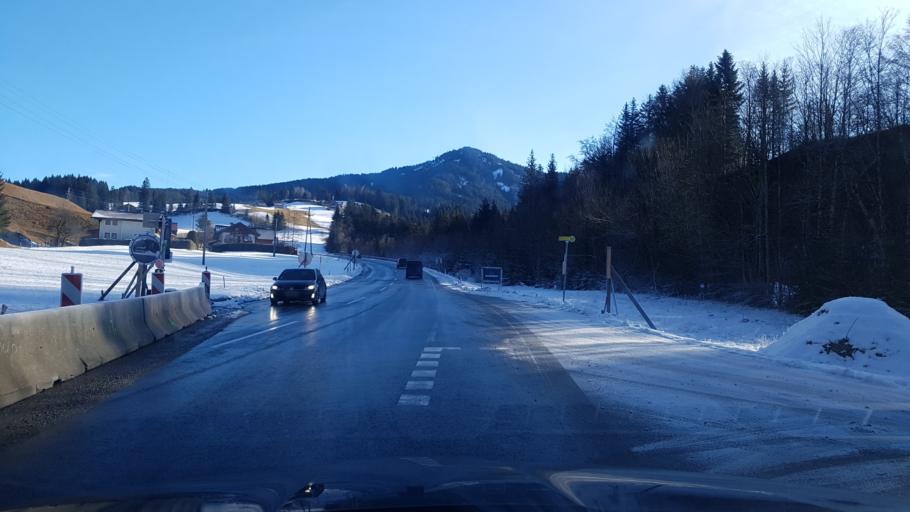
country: AT
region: Salzburg
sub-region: Politischer Bezirk Hallein
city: Abtenau
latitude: 47.5803
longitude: 13.4407
